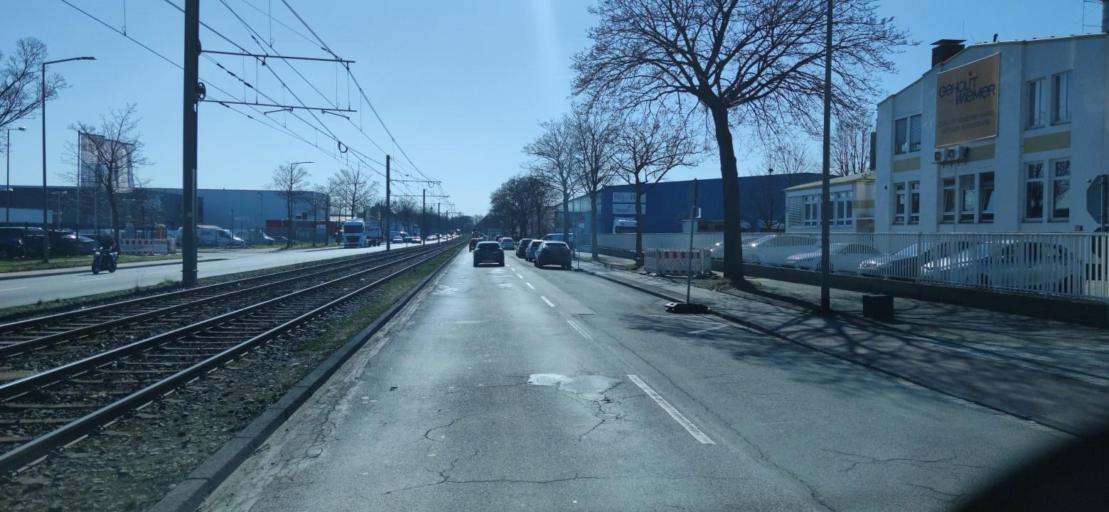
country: DE
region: North Rhine-Westphalia
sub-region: Regierungsbezirk Dusseldorf
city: Hochfeld
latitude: 51.3923
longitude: 6.7525
